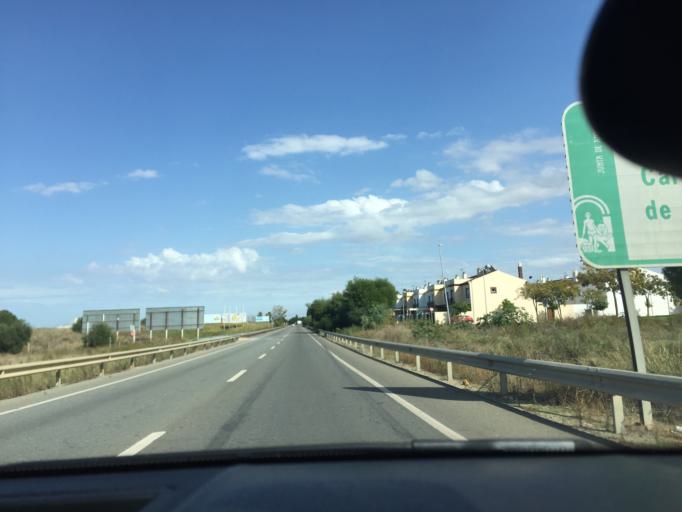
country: ES
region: Andalusia
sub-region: Provincia de Sevilla
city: Coria del Rio
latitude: 37.2991
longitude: -6.0489
